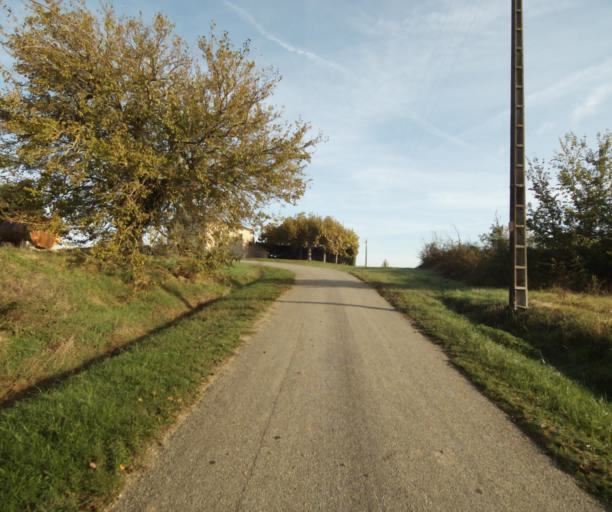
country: FR
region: Midi-Pyrenees
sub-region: Departement de la Haute-Garonne
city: Villemur-sur-Tarn
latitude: 43.9232
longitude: 1.4922
